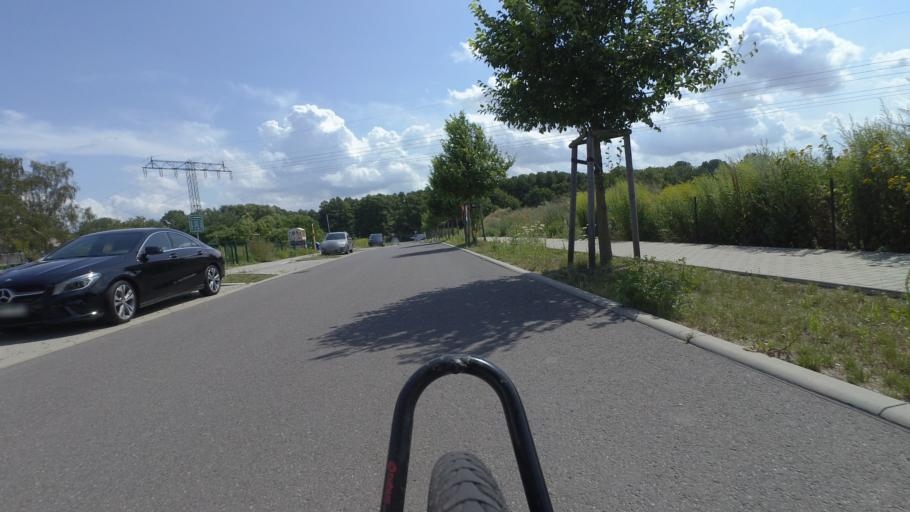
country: DE
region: Brandenburg
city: Grossbeeren
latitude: 52.3475
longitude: 13.3025
